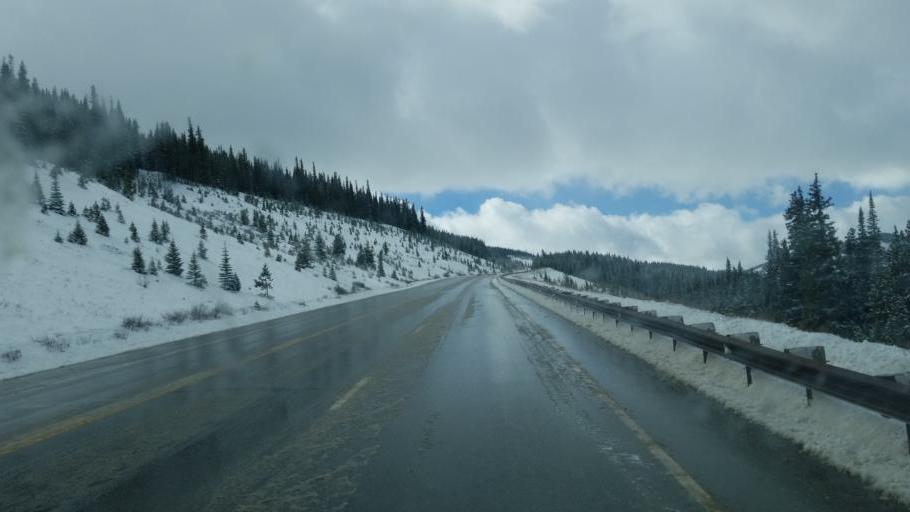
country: US
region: Colorado
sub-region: Summit County
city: Breckenridge
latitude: 39.4434
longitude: -106.1554
